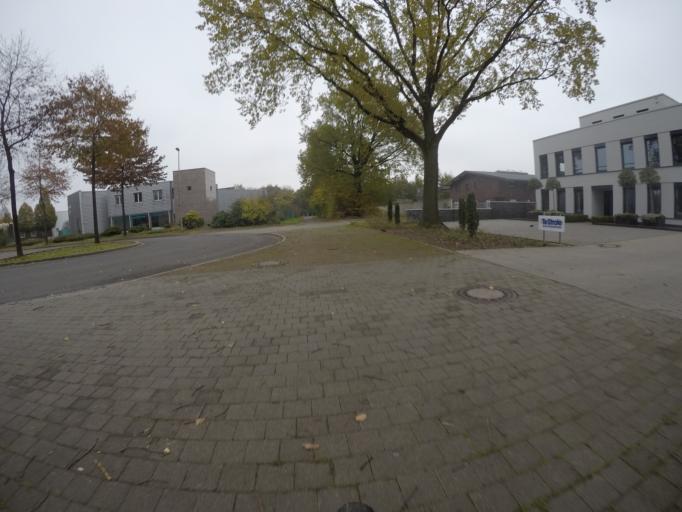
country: DE
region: North Rhine-Westphalia
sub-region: Regierungsbezirk Dusseldorf
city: Bocholt
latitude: 51.8151
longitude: 6.5758
